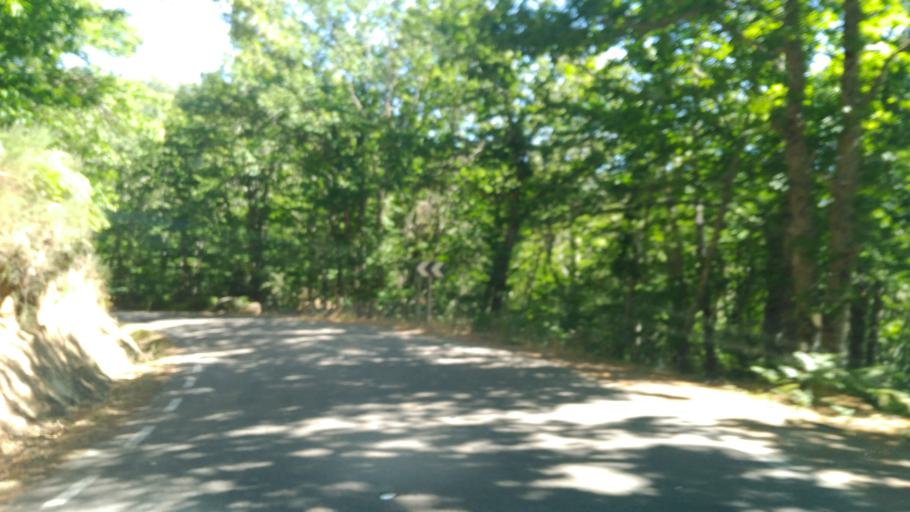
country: ES
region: Castille and Leon
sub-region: Provincia de Salamanca
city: San Martin del Castanar
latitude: 40.5270
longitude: -6.0763
